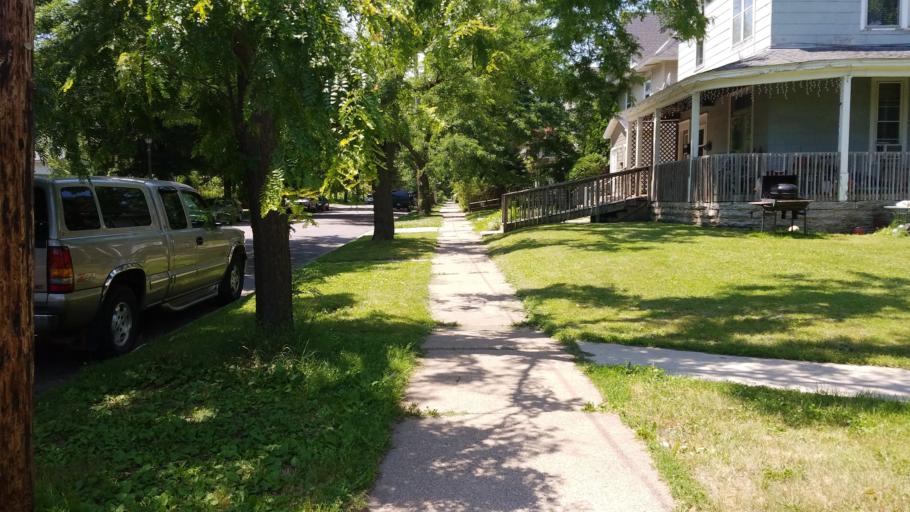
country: US
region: Minnesota
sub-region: Ramsey County
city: Saint Paul
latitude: 44.9276
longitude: -93.0737
